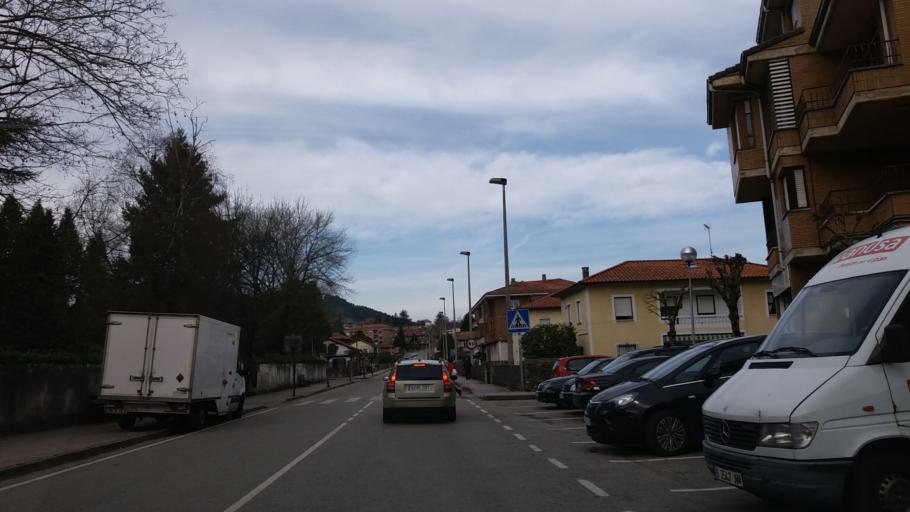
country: ES
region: Cantabria
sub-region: Provincia de Cantabria
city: Reocin
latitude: 43.3603
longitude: -4.0879
